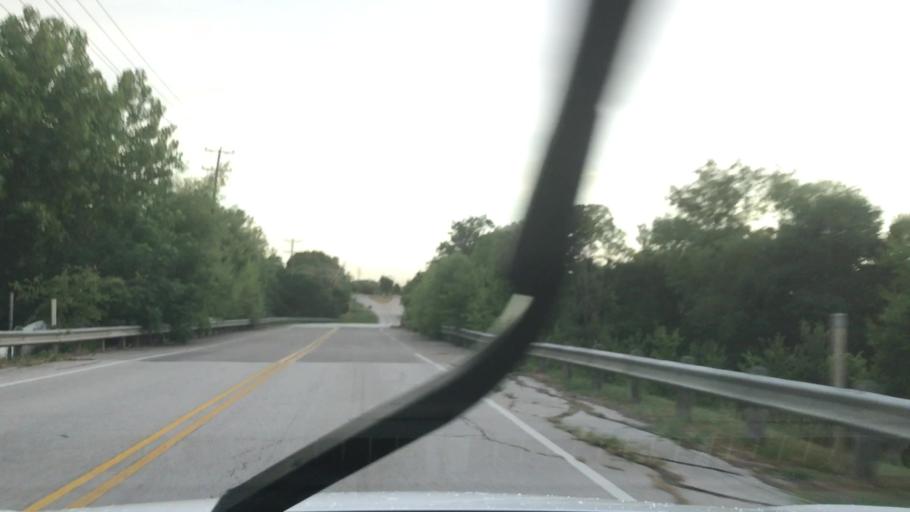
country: US
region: Texas
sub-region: Dallas County
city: Balch Springs
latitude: 32.7111
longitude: -96.5541
